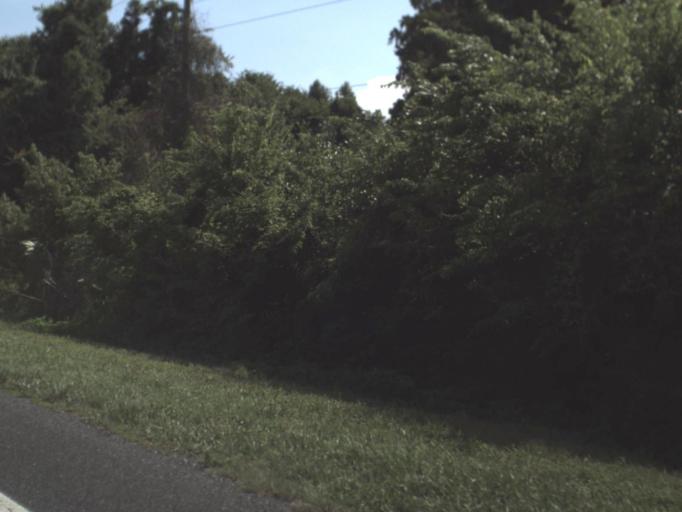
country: US
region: Florida
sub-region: Marion County
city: Citra
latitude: 29.4361
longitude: -82.1099
